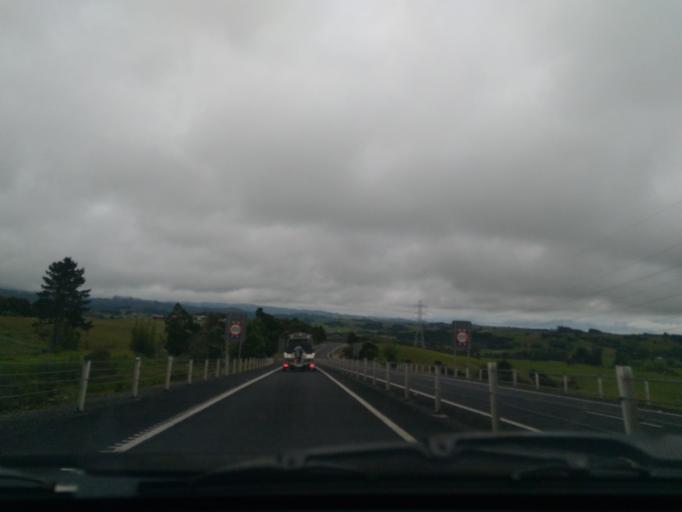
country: NZ
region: Northland
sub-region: Whangarei
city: Ruakaka
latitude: -36.0449
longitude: 174.4178
